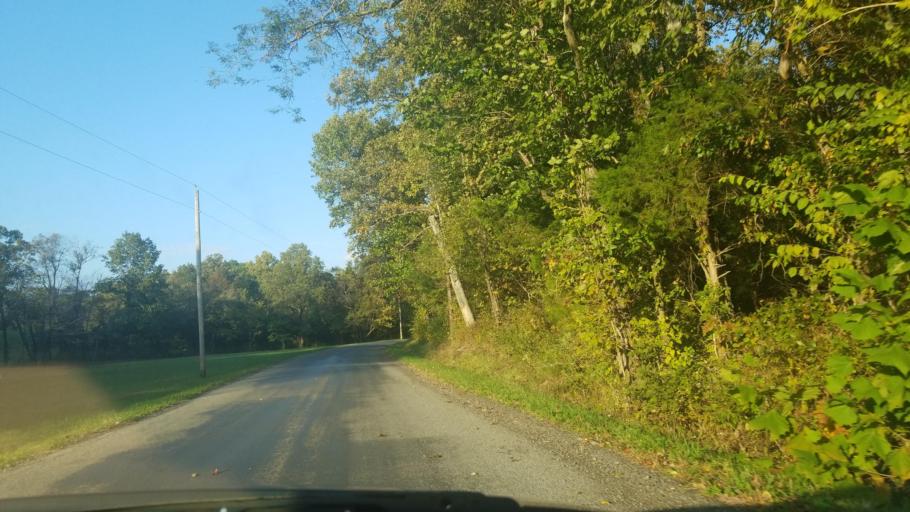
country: US
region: Illinois
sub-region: Williamson County
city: Marion
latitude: 37.7637
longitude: -88.7788
